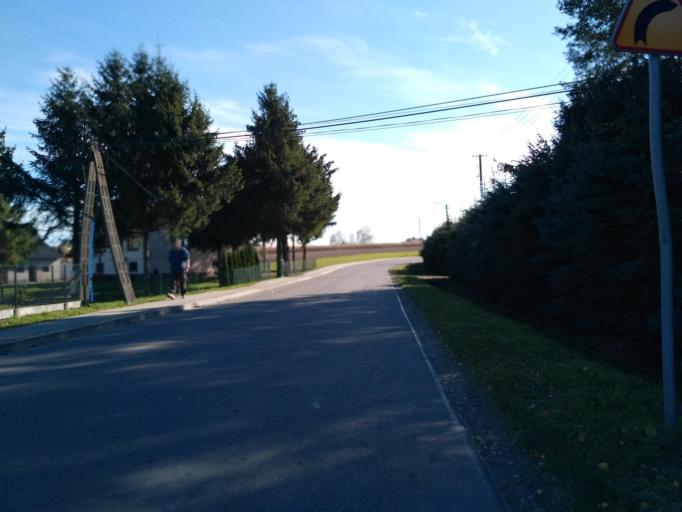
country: PL
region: Subcarpathian Voivodeship
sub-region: Powiat ropczycko-sedziszowski
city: Iwierzyce
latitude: 50.0253
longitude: 21.7680
